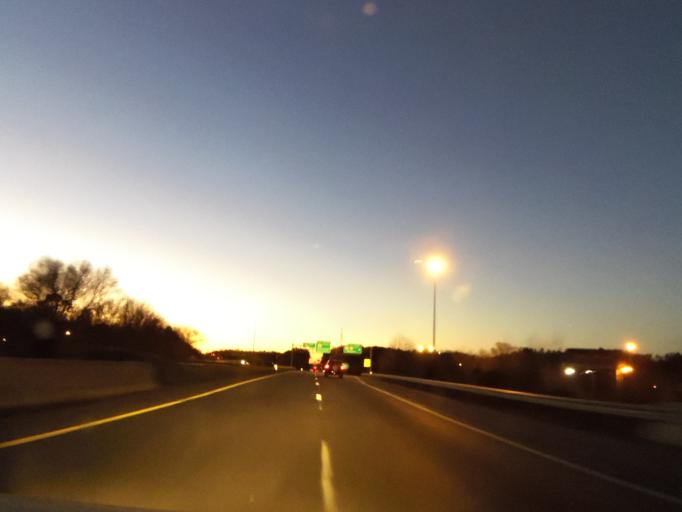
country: US
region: Tennessee
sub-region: Cocke County
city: Newport
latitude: 35.9682
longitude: -83.2488
